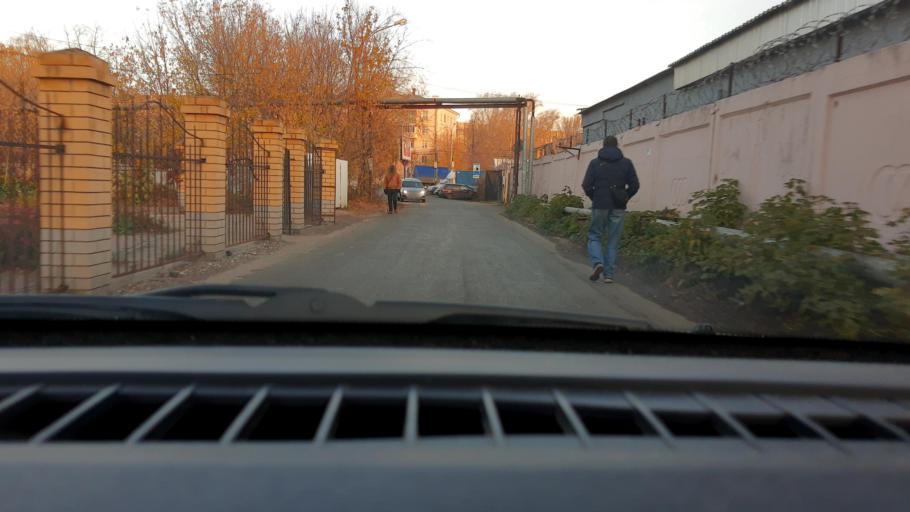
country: RU
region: Nizjnij Novgorod
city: Nizhniy Novgorod
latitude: 56.3139
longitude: 43.9043
